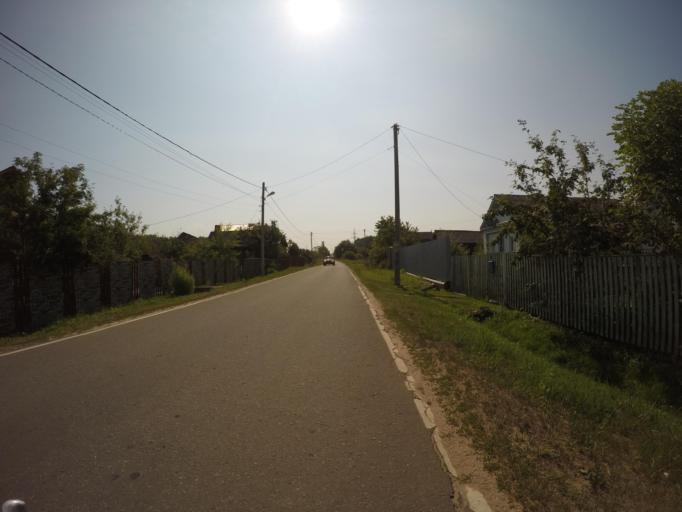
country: RU
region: Moskovskaya
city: Rechitsy
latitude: 55.6302
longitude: 38.5131
